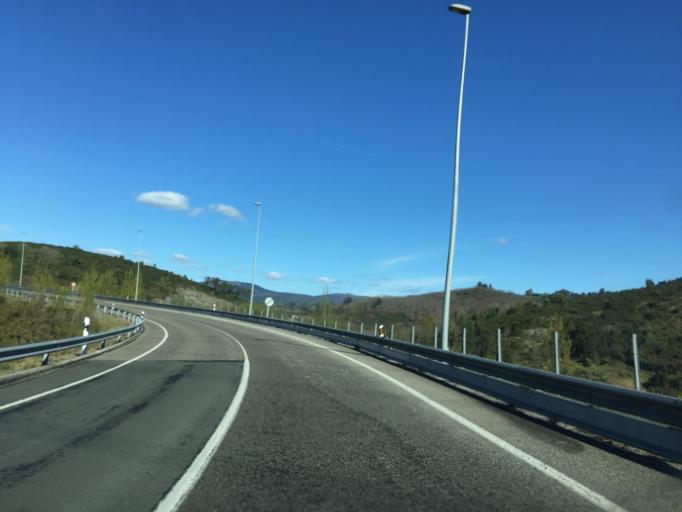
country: ES
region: Asturias
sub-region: Province of Asturias
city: Llanera
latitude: 43.3633
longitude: -5.9483
